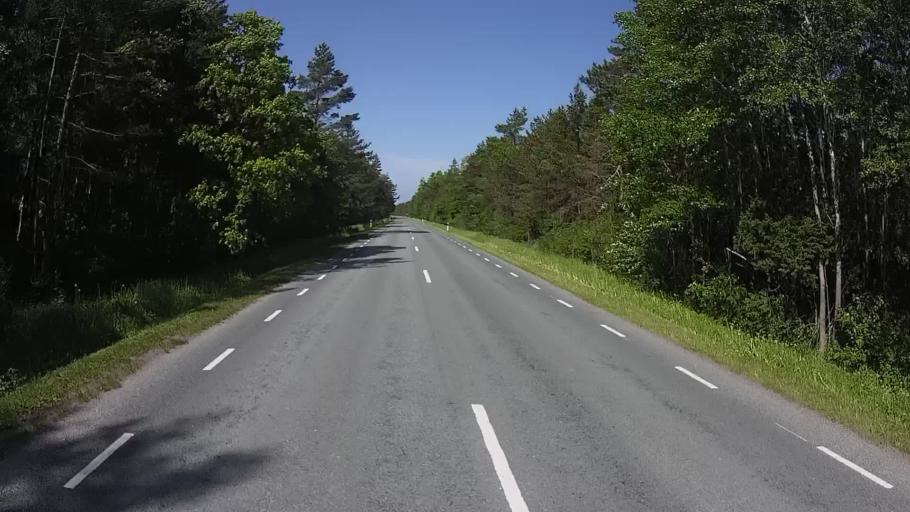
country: EE
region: Saare
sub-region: Kuressaare linn
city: Kuressaare
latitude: 58.3541
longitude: 22.4428
